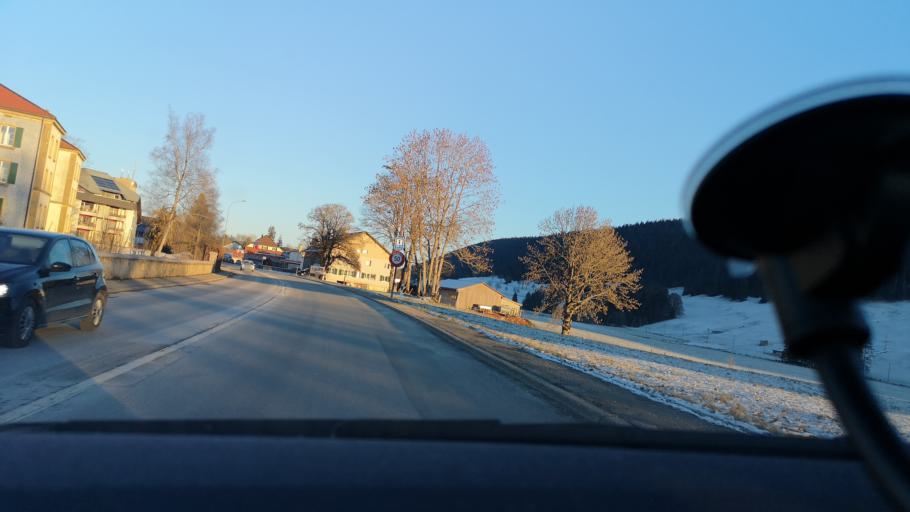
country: CH
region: Vaud
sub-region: Jura-Nord vaudois District
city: Sainte-Croix
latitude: 46.9026
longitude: 6.4713
